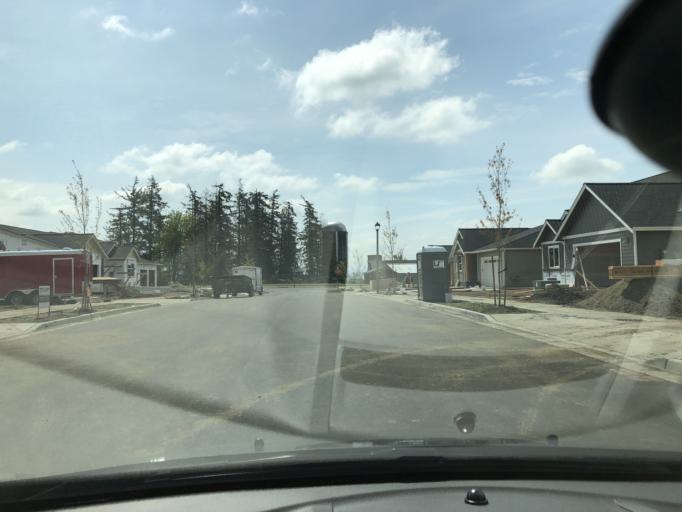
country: US
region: Washington
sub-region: Whatcom County
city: Lynden
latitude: 48.9606
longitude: -122.4055
